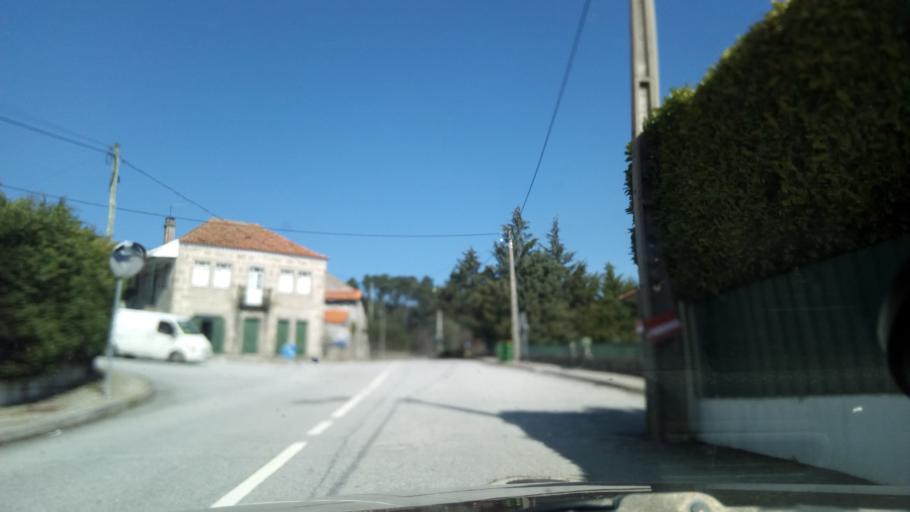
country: PT
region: Guarda
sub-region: Fornos de Algodres
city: Fornos de Algodres
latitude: 40.6314
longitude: -7.5346
